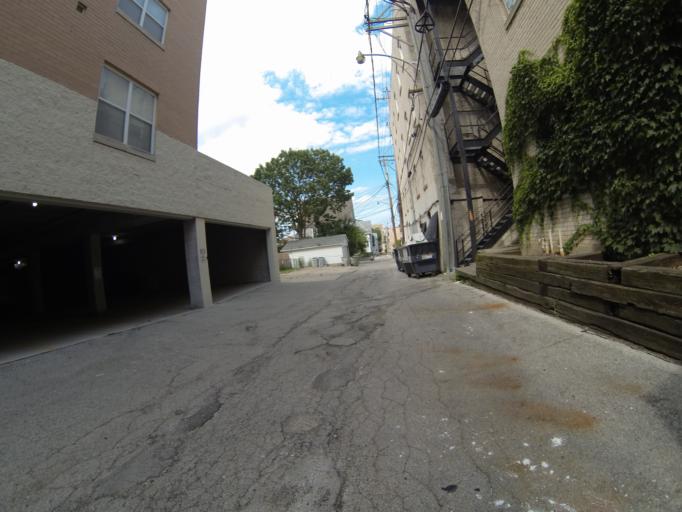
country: US
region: Wisconsin
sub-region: Milwaukee County
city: Milwaukee
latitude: 43.0553
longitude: -87.8893
